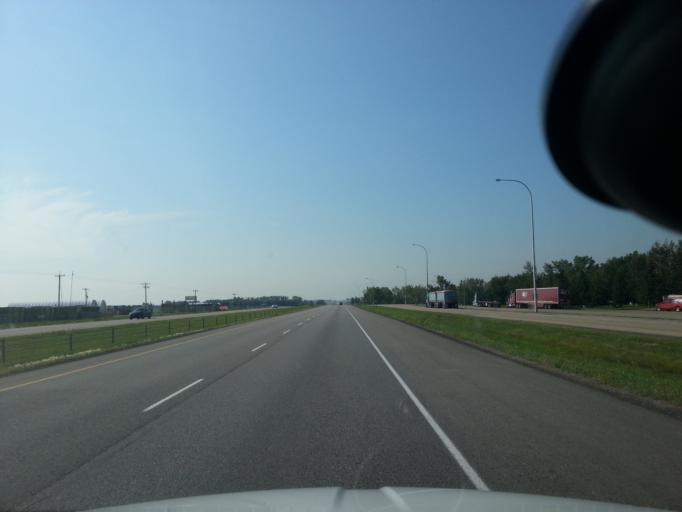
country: CA
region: Alberta
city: Olds
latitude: 51.9327
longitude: -114.0255
